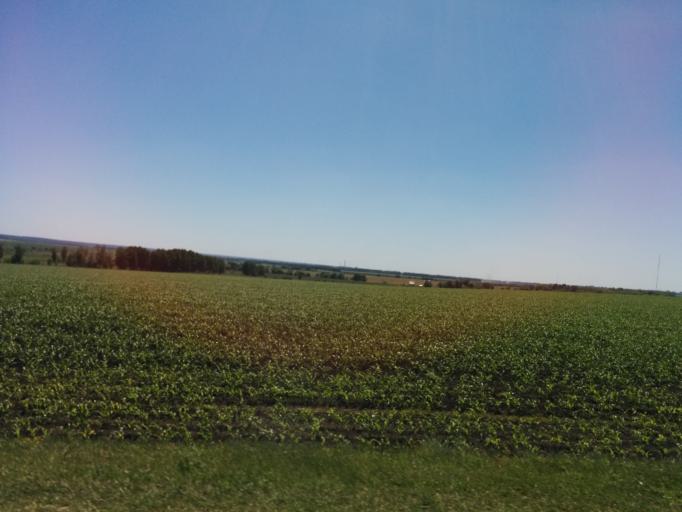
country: RU
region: Tambov
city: Donskoye
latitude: 52.8361
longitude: 41.4266
